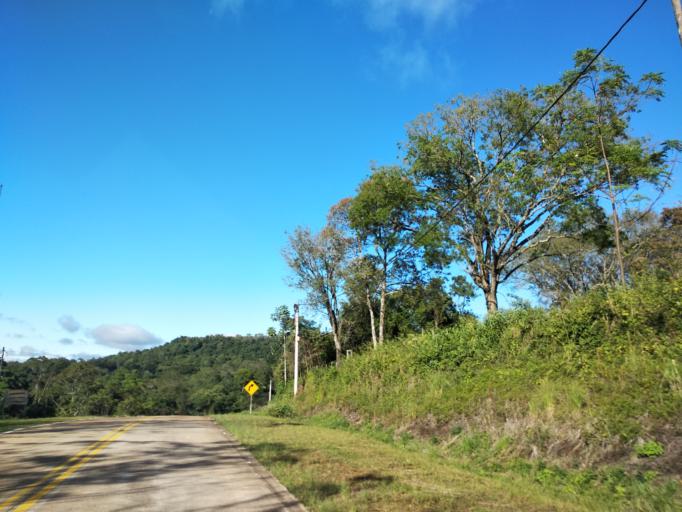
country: AR
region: Misiones
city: Cerro Cora
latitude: -27.4514
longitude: -55.5651
